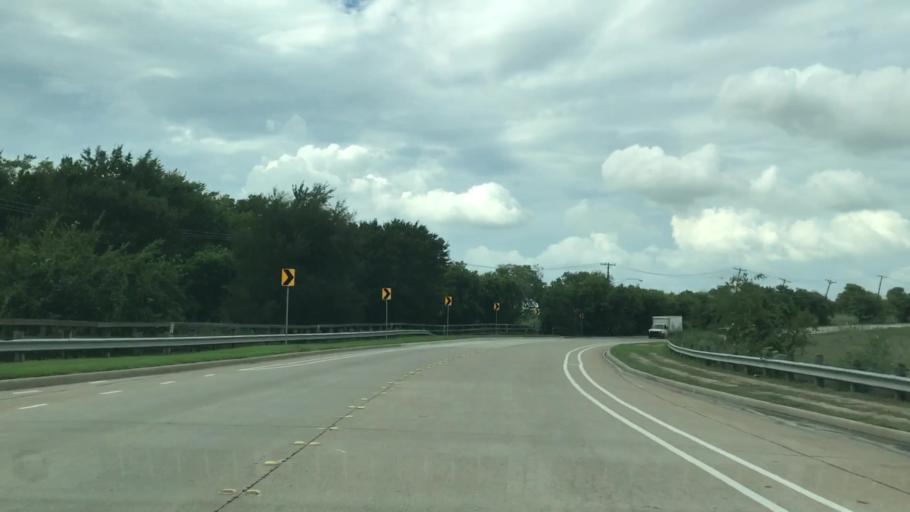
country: US
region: Texas
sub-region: Collin County
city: Frisco
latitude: 33.1424
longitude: -96.8250
